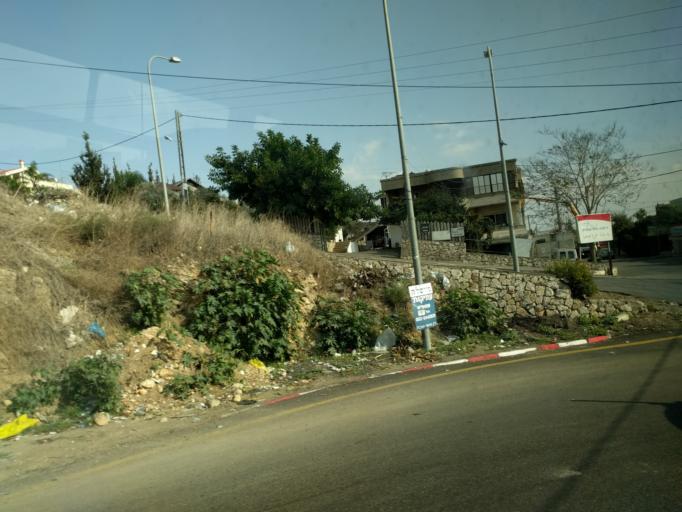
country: IL
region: Haifa
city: Daliyat el Karmil
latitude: 32.7142
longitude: 35.0697
